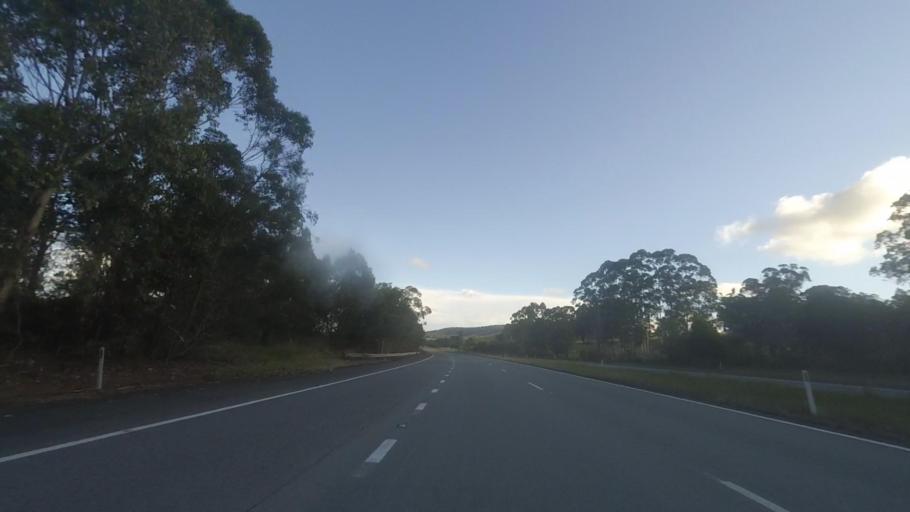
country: AU
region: New South Wales
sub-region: Great Lakes
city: Nabiac
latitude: -32.2532
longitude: 152.3235
